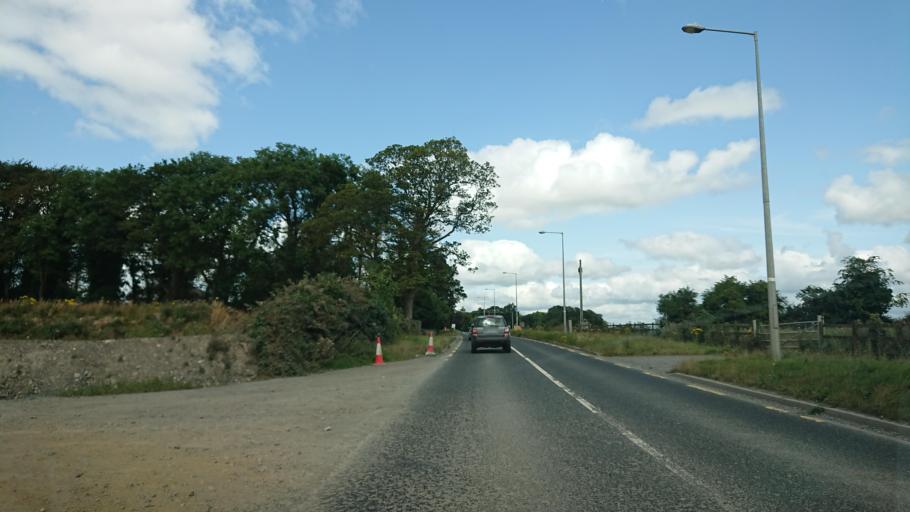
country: IE
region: Leinster
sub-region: Kildare
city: Sallins
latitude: 53.2615
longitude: -6.6689
